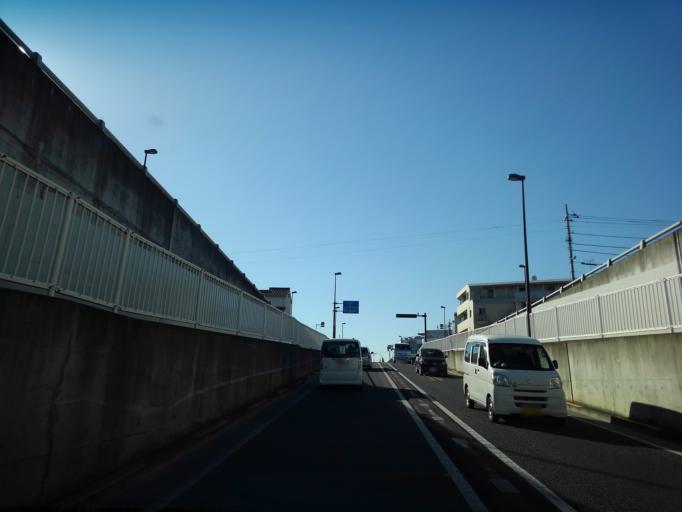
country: JP
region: Tokyo
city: Hino
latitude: 35.7080
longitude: 139.3782
